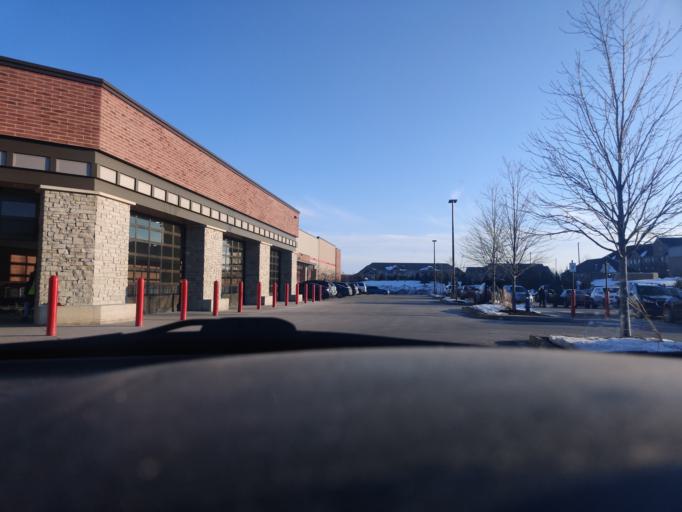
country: US
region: Wisconsin
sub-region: Kenosha County
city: Pleasant Prairie
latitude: 42.5645
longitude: -87.9198
